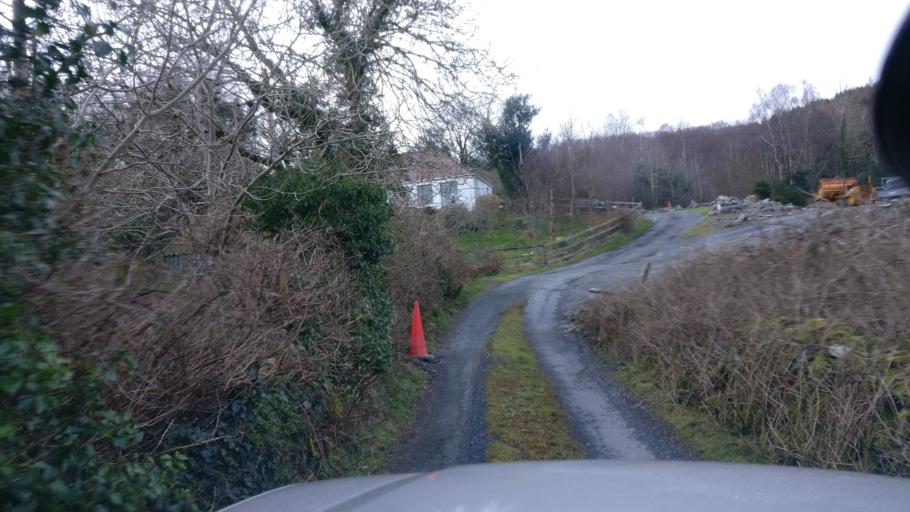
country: IE
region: Connaught
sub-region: County Galway
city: Oughterard
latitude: 53.5186
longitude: -9.4394
